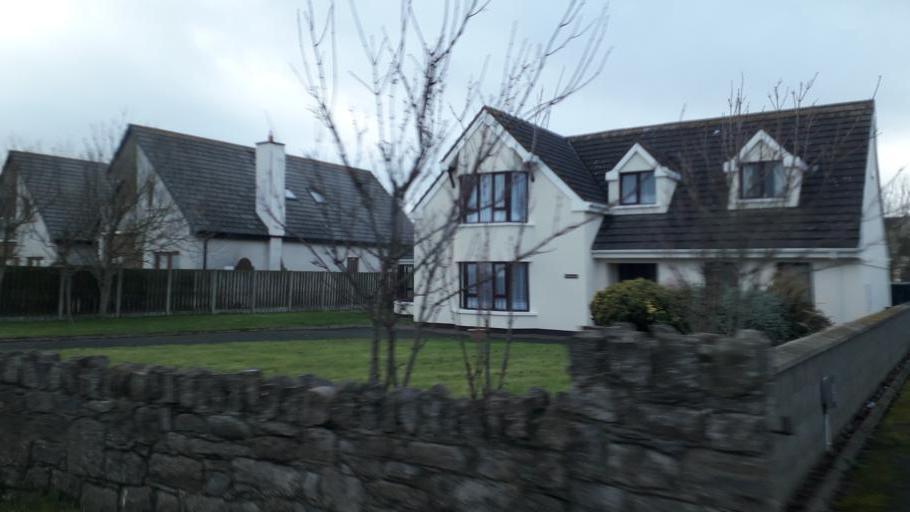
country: IE
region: Leinster
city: An Ros
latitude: 53.5203
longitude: -6.0792
